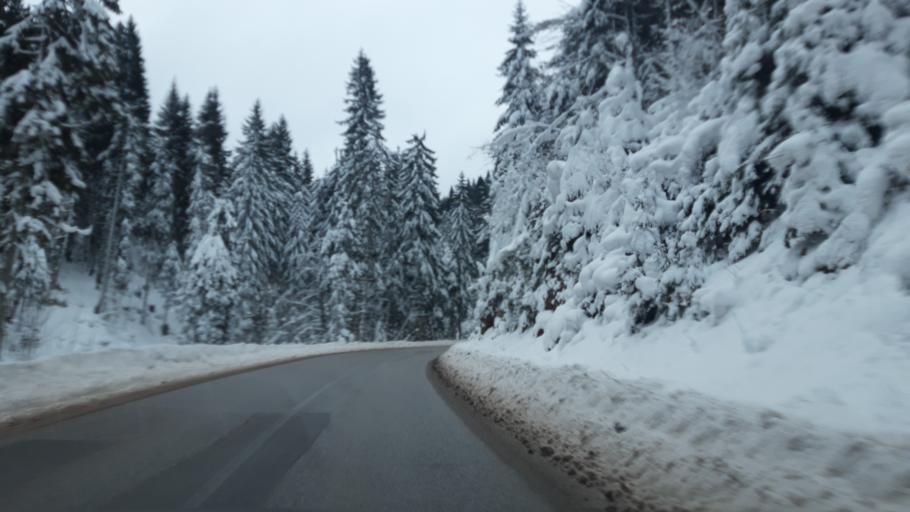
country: BA
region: Republika Srpska
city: Koran
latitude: 43.7482
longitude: 18.5556
